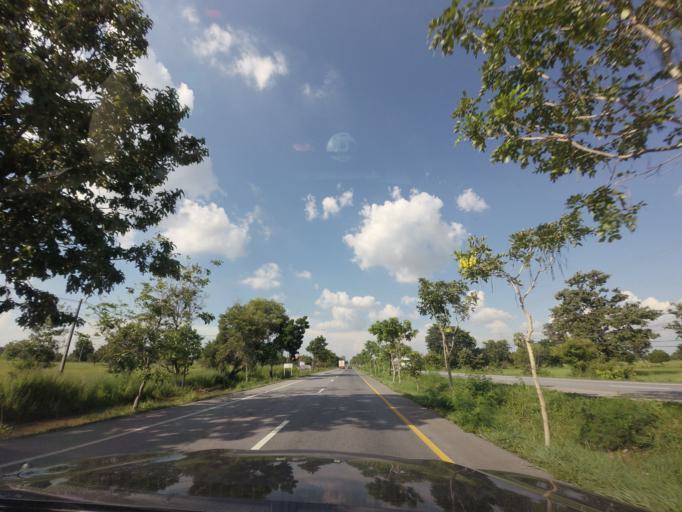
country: TH
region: Nakhon Ratchasima
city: Bua Lai
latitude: 15.7125
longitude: 102.5885
